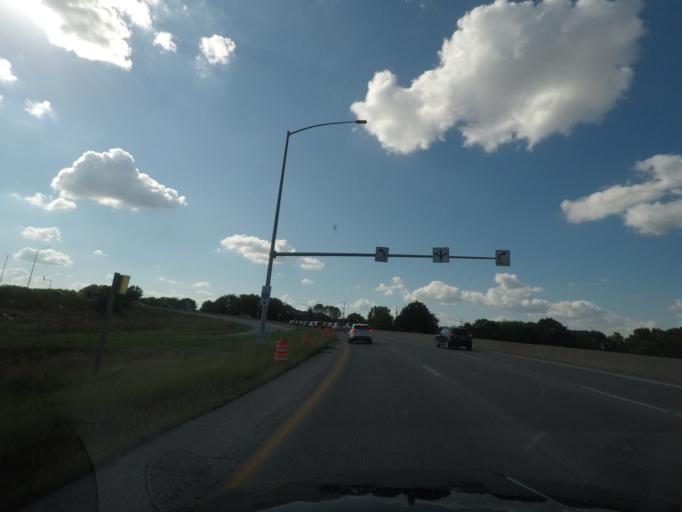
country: US
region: Iowa
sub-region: Dallas County
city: Waukee
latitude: 41.5931
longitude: -93.8073
